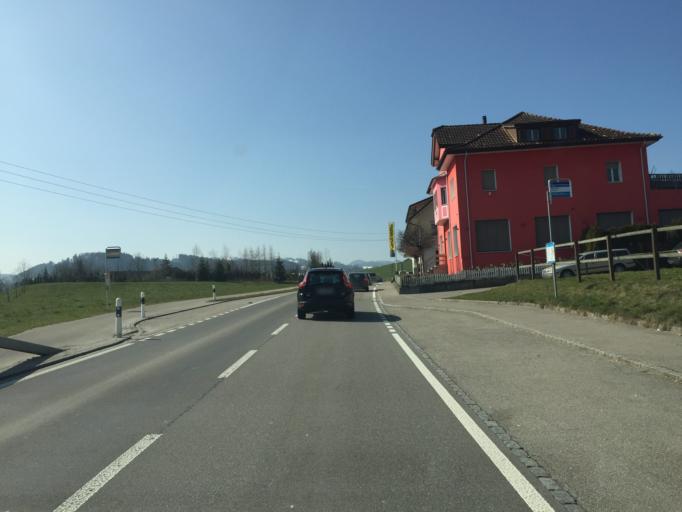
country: CH
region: Saint Gallen
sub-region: Wahlkreis Toggenburg
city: Lutisburg
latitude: 47.3869
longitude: 9.0755
